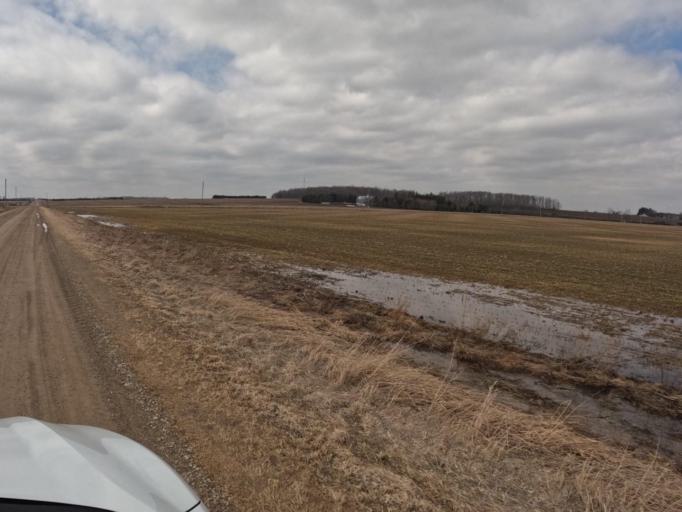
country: CA
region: Ontario
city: Shelburne
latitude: 44.0488
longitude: -80.2995
